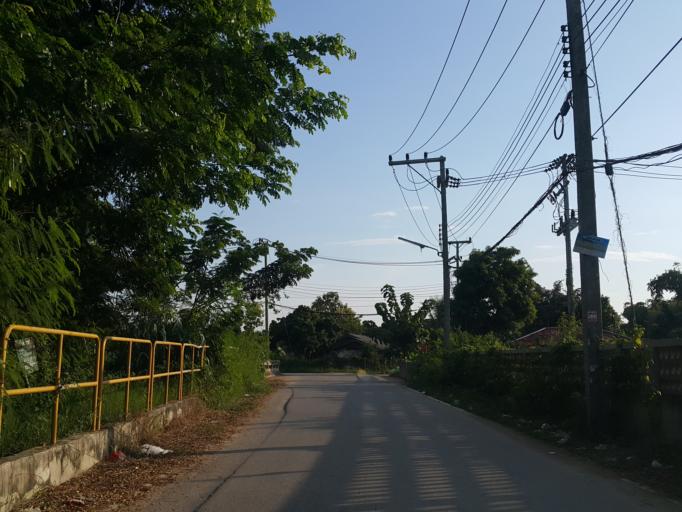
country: TH
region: Chiang Mai
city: San Kamphaeng
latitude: 18.7479
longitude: 99.0933
